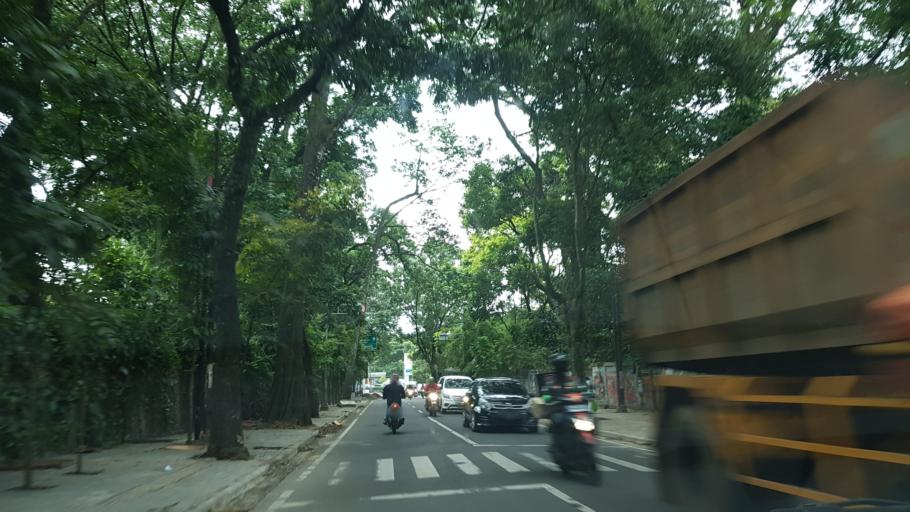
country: ID
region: West Java
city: Bandung
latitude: -6.8924
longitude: 107.6082
